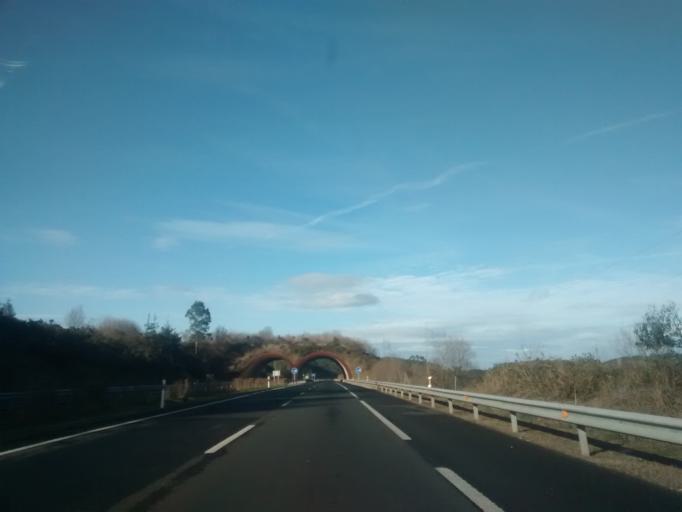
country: ES
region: Cantabria
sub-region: Provincia de Cantabria
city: Cabezon de la Sal
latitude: 43.3217
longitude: -4.2767
